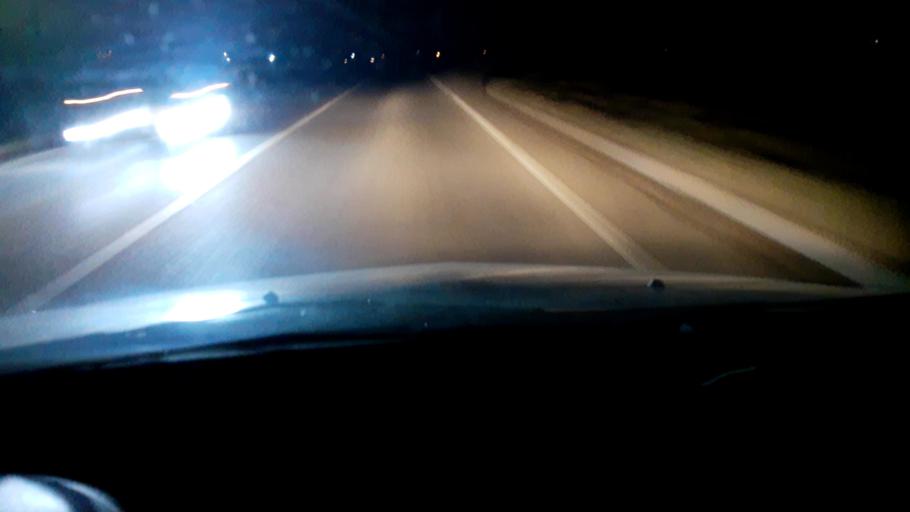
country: RU
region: Bashkortostan
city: Kabakovo
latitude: 54.7380
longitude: 56.2032
